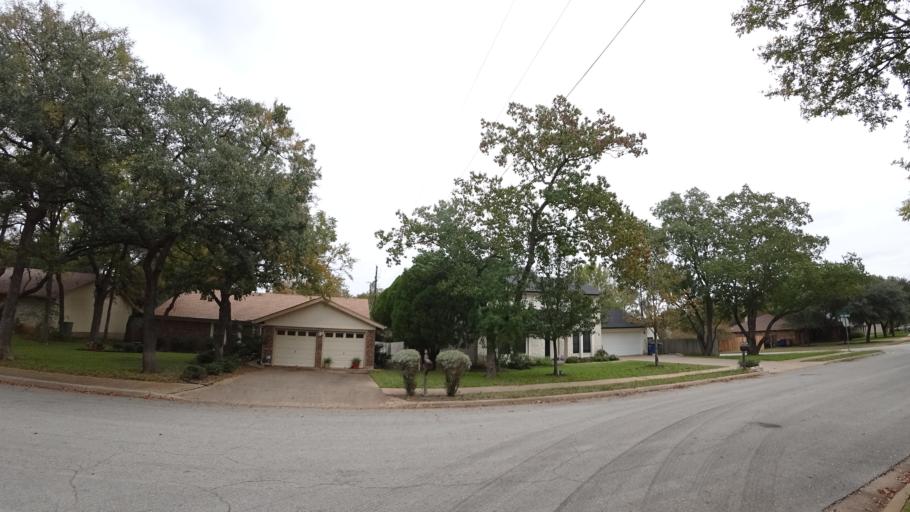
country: US
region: Texas
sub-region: Travis County
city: Wells Branch
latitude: 30.4319
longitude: -97.7157
